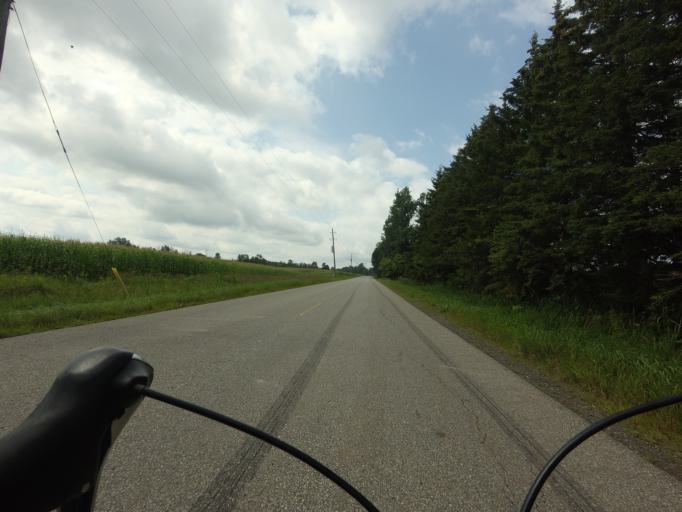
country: CA
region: Ontario
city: Brockville
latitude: 44.7751
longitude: -75.7277
